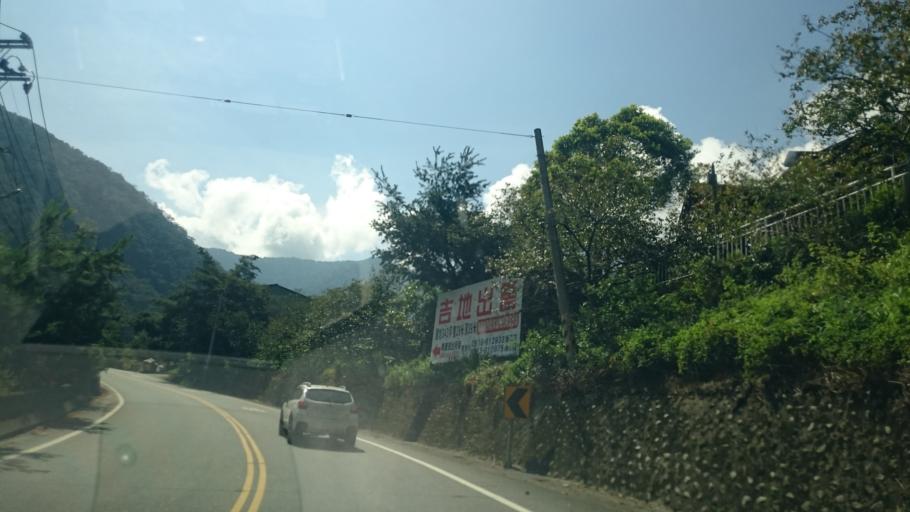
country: TW
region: Taiwan
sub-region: Nantou
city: Puli
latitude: 24.0042
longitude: 121.0642
